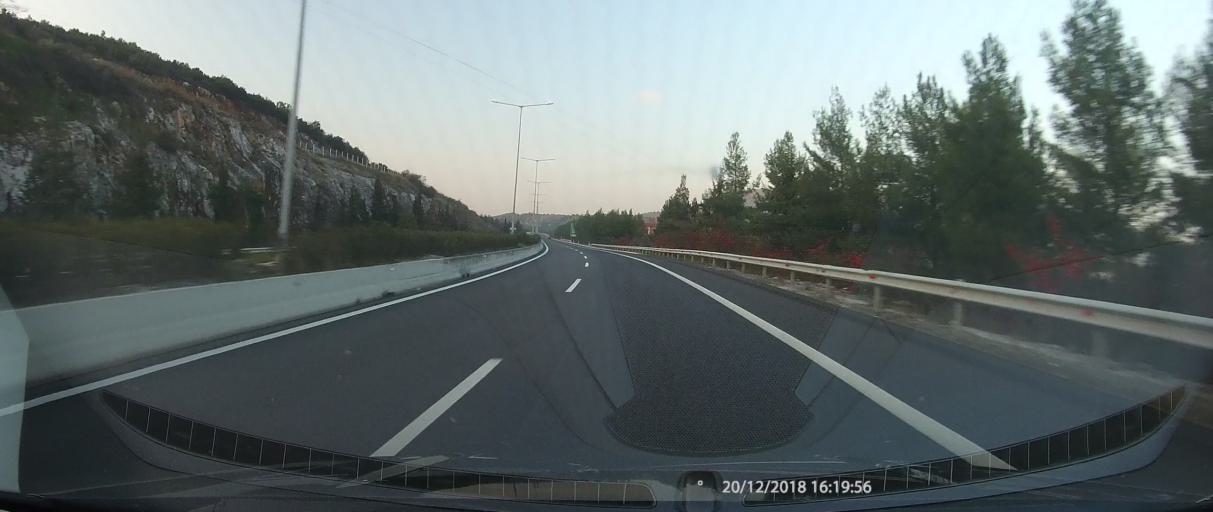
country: GR
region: Thessaly
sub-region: Nomos Magnisias
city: Pteleos
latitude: 39.0194
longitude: 22.9156
